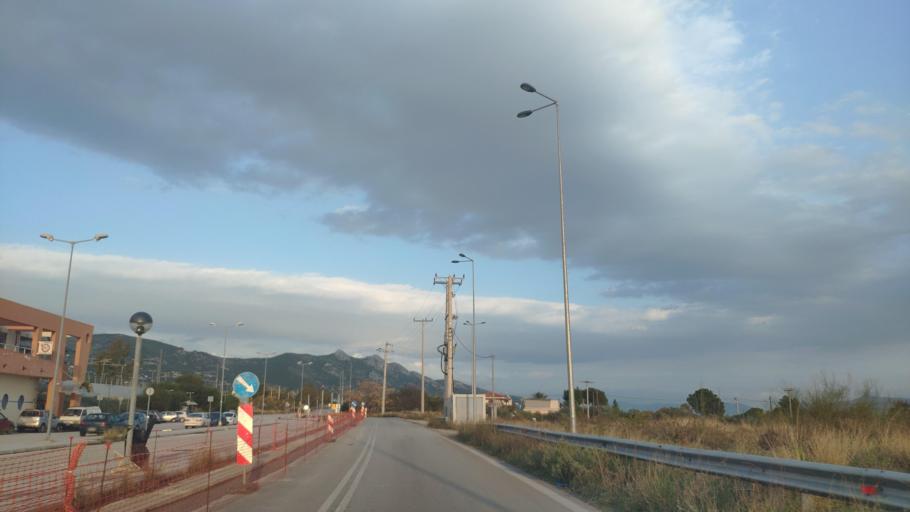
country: GR
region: Attica
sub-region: Nomarchia Dytikis Attikis
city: Nea Peramos
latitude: 38.0127
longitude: 23.4141
